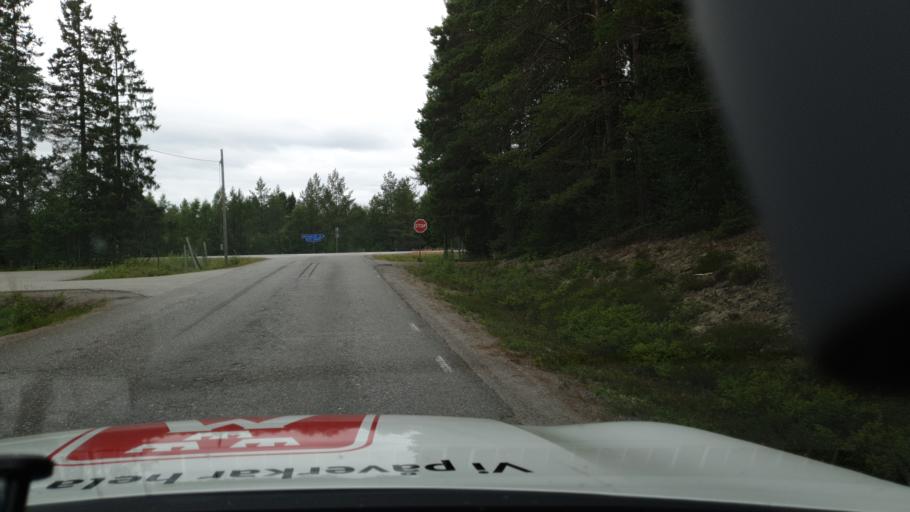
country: SE
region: Vaesterbotten
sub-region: Robertsfors Kommun
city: Robertsfors
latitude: 63.9990
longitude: 20.7909
